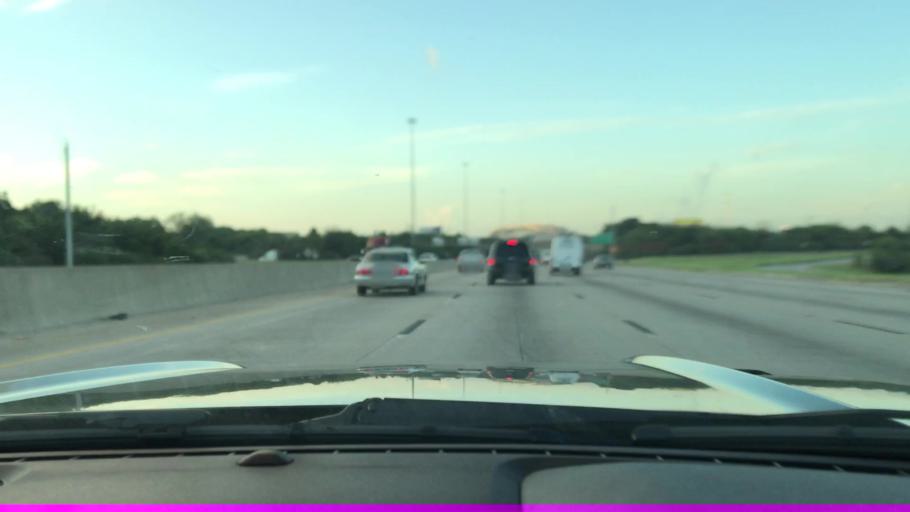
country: US
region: Texas
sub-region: Harris County
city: Galena Park
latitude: 29.7421
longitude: -95.2650
